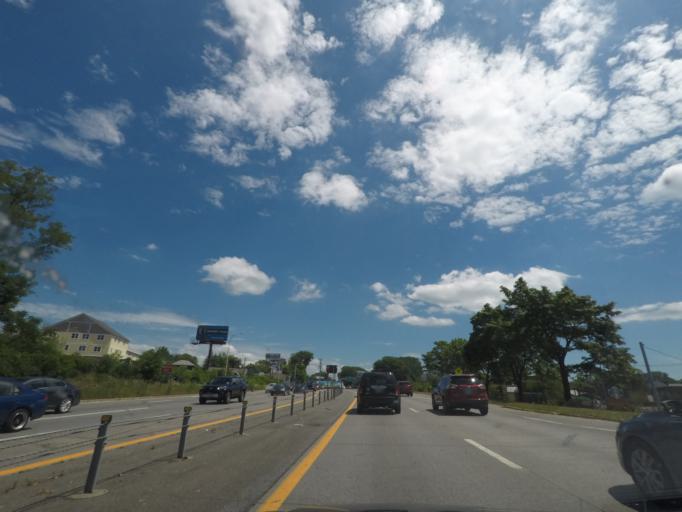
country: US
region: New York
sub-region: Schenectady County
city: Schenectady
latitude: 42.7836
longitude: -73.9147
